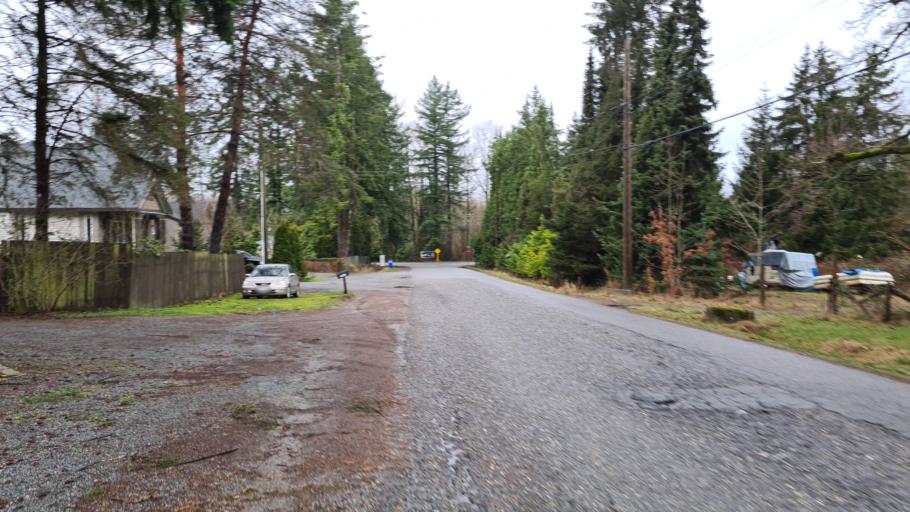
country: CA
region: British Columbia
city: Walnut Grove
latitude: 49.1384
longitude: -122.6597
